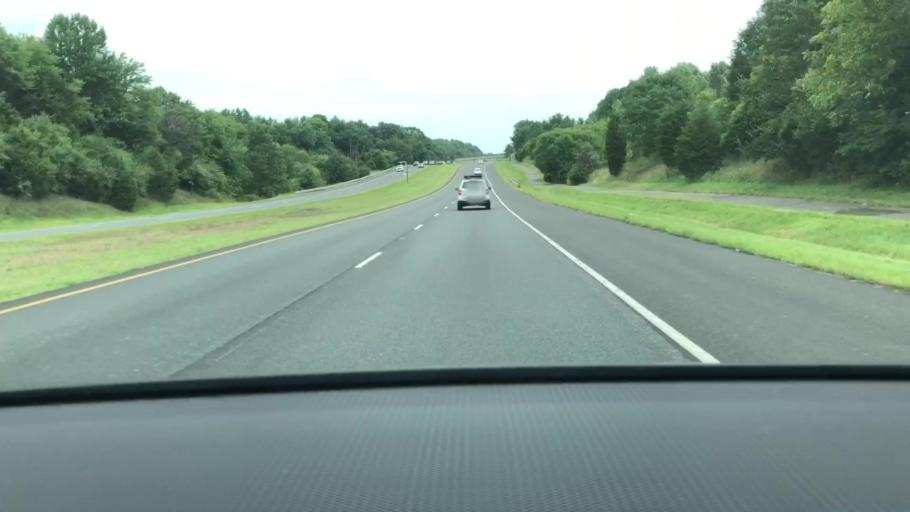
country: US
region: Virginia
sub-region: Fairfax County
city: Oak Hill
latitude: 38.9242
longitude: -77.3947
